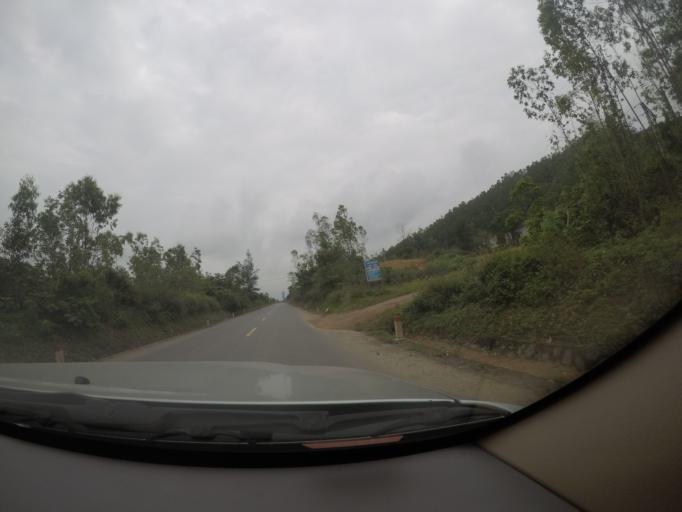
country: VN
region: Quang Binh
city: Quan Hau
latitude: 17.2732
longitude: 106.6573
